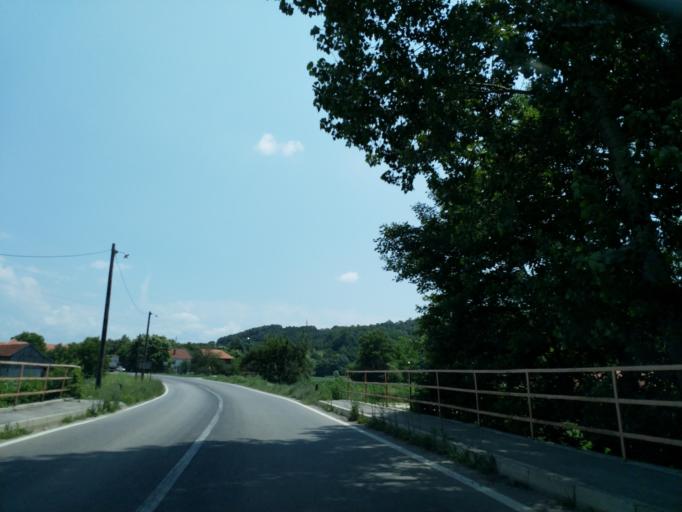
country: RS
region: Central Serbia
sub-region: Toplicki Okrug
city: Blace
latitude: 43.3067
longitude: 21.2488
